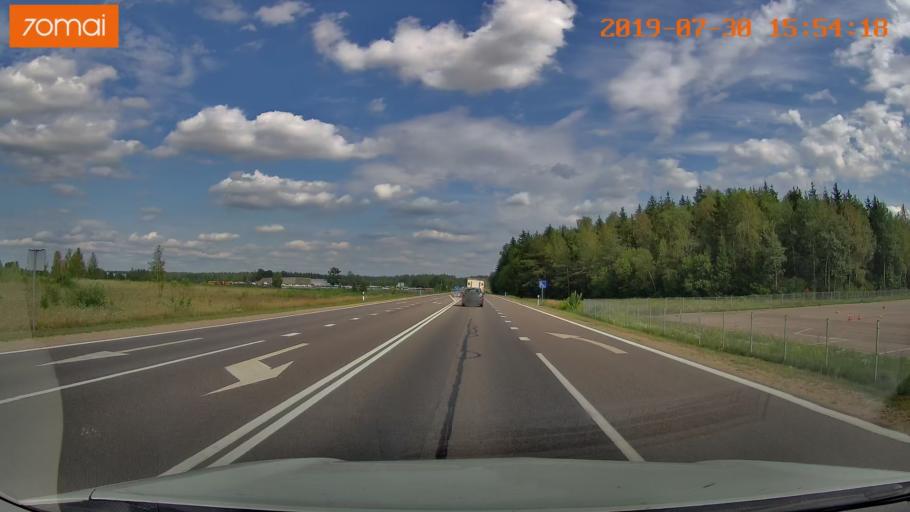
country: LT
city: Lentvaris
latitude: 54.6200
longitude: 25.0567
